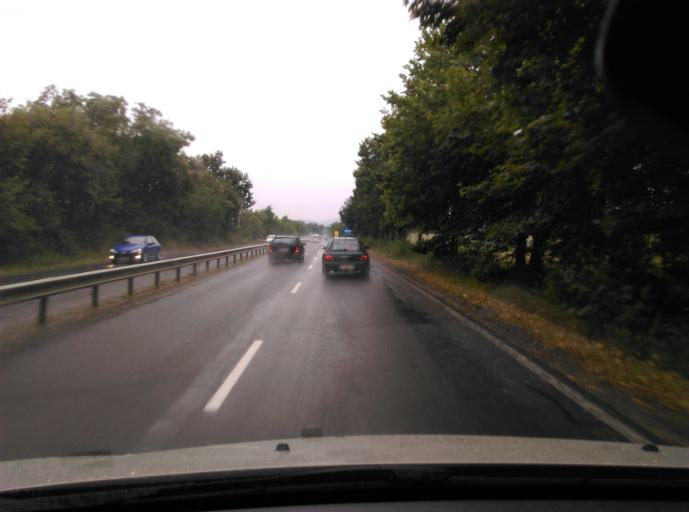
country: BG
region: Burgas
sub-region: Obshtina Burgas
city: Burgas
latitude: 42.4349
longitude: 27.4884
